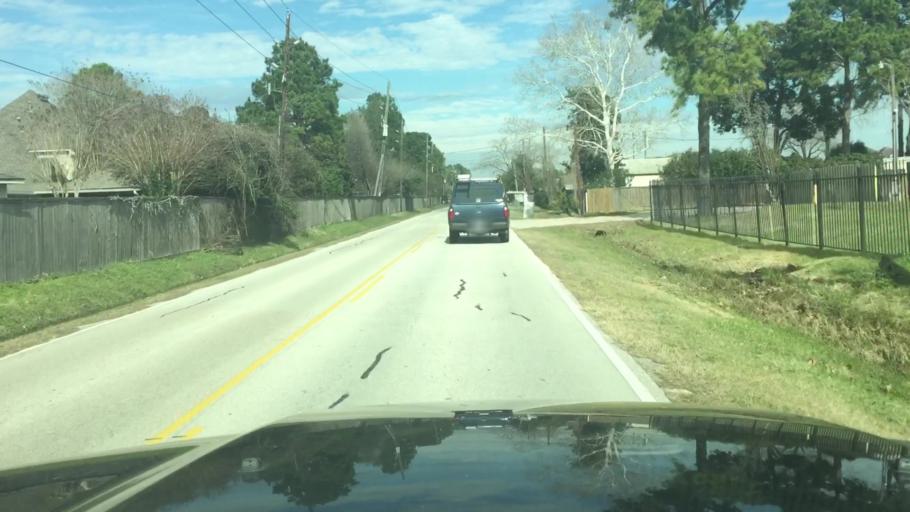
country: US
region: Texas
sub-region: Harris County
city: Oak Cliff Place
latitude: 29.8343
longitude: -95.6751
